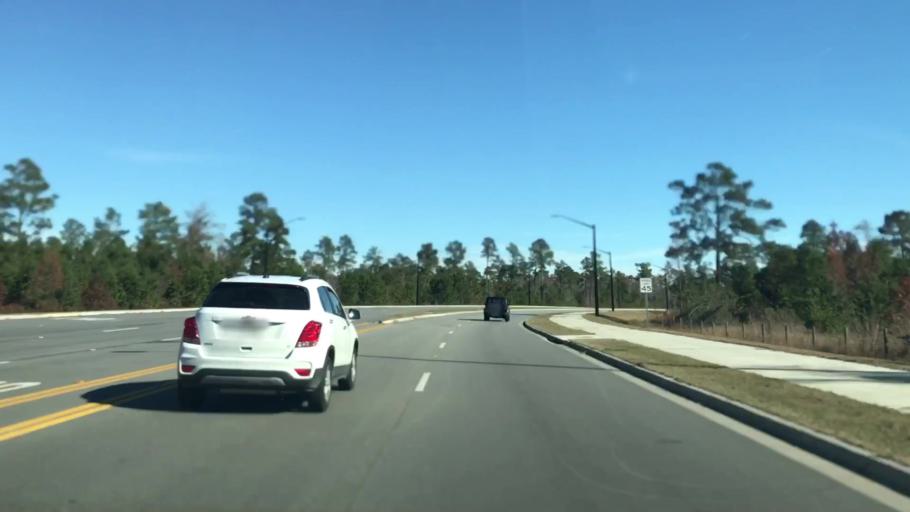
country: US
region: South Carolina
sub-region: Dorchester County
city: Summerville
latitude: 33.0496
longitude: -80.1725
